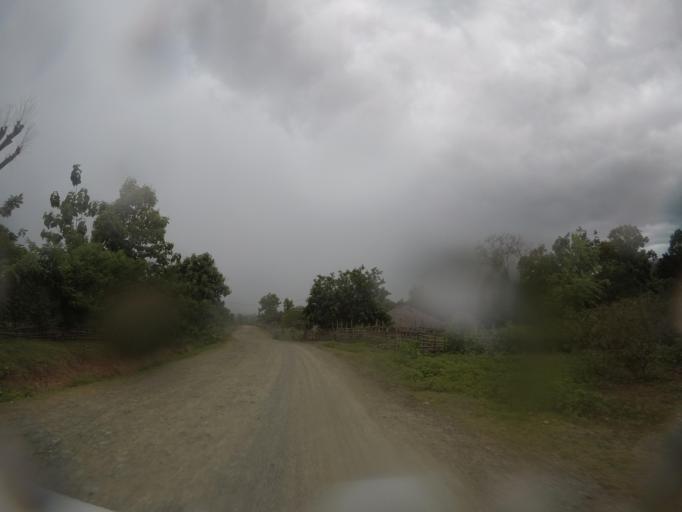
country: TL
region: Bobonaro
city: Maliana
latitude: -8.8541
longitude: 125.0859
